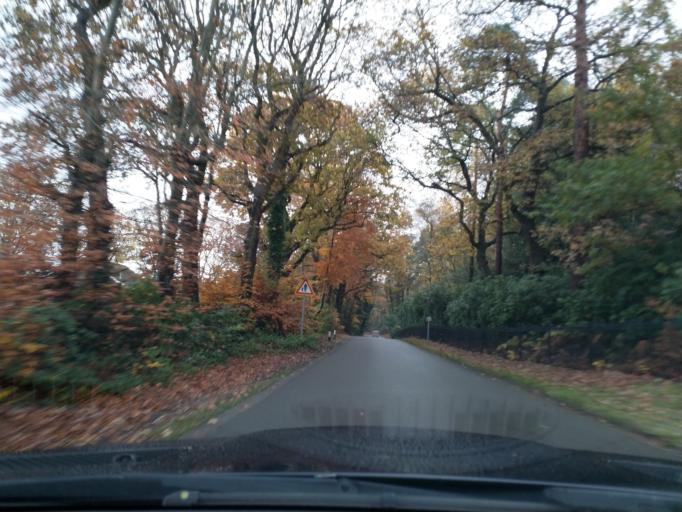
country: GB
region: England
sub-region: Surrey
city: Frimley
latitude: 51.3060
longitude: -0.7209
